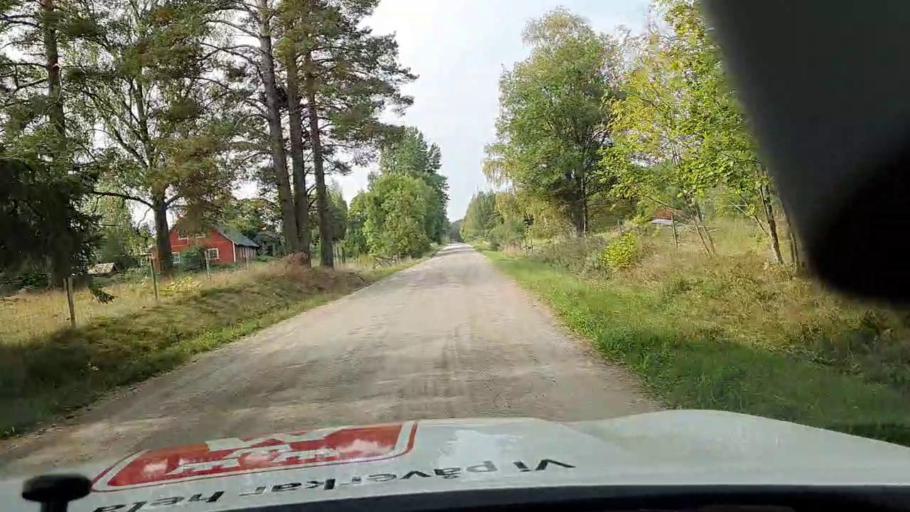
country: SE
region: Soedermanland
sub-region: Nykopings Kommun
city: Stigtomta
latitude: 58.8115
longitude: 16.8130
